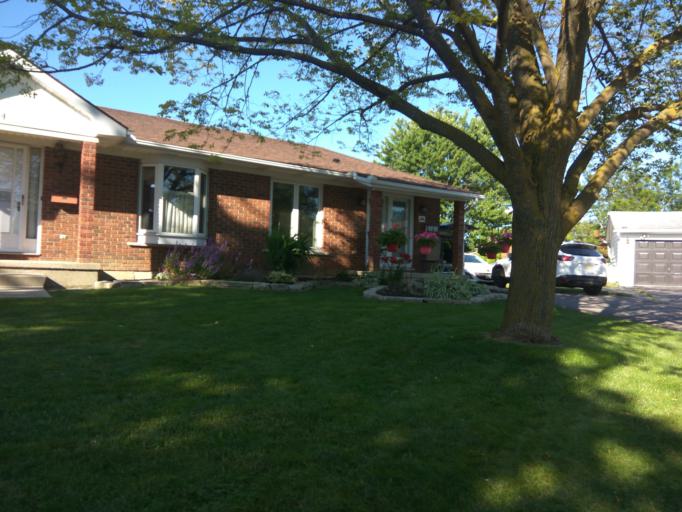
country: CA
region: Ontario
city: Stratford
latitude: 43.3624
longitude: -81.0059
